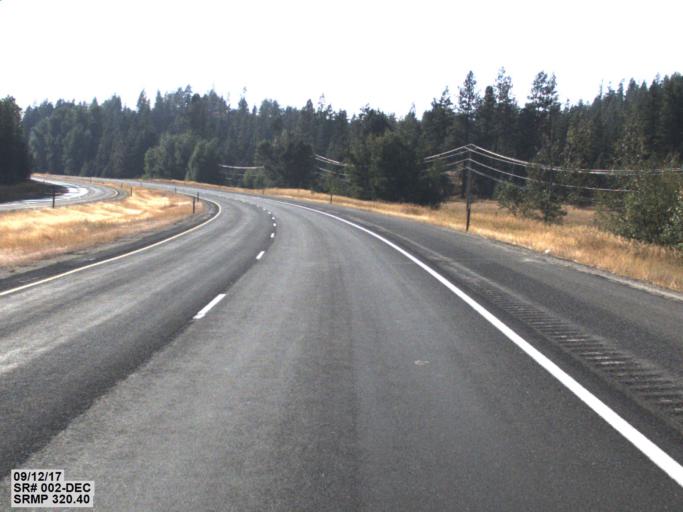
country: US
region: Washington
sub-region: Spokane County
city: Deer Park
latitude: 48.0987
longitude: -117.2972
